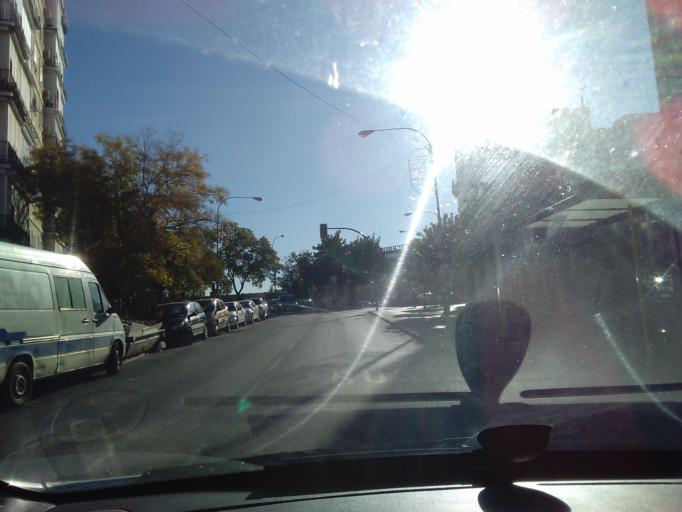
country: ES
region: Andalusia
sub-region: Provincia de Sevilla
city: Sevilla
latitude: 37.3904
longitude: -5.9674
